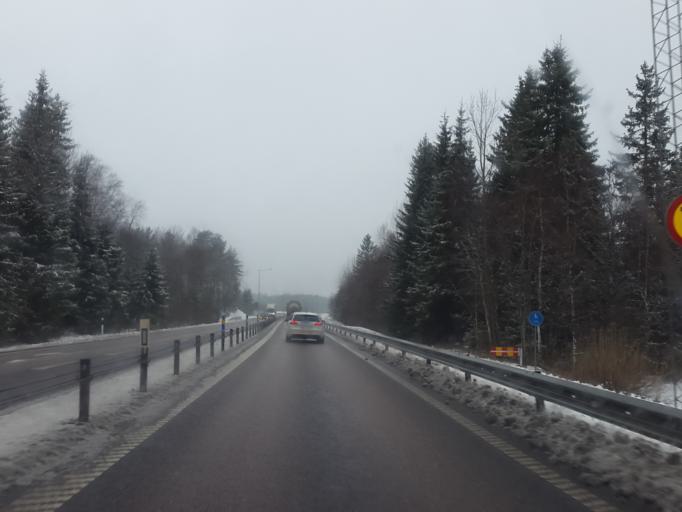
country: SE
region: Joenkoeping
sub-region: Mullsjo Kommun
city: Mullsjoe
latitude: 57.7753
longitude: 13.6845
